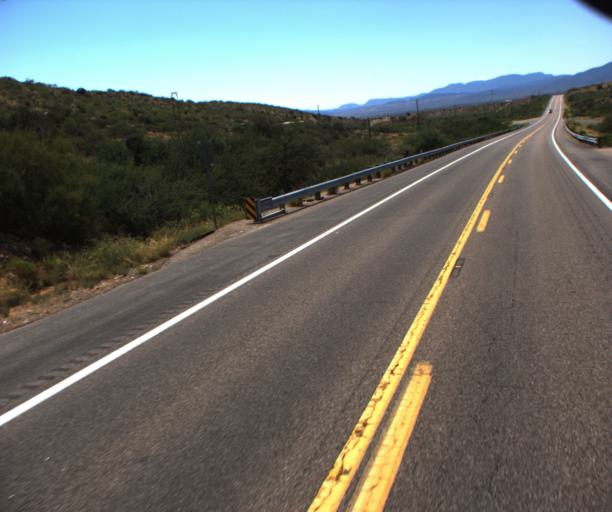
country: US
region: Arizona
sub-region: Gila County
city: Globe
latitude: 33.4499
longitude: -110.7209
